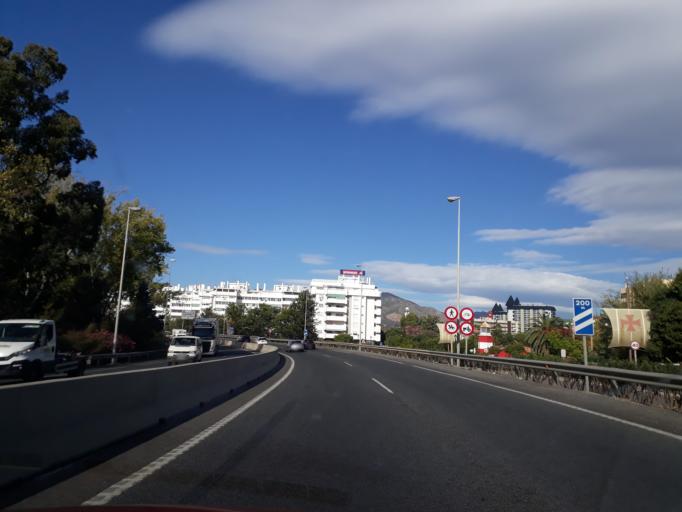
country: ES
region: Andalusia
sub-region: Provincia de Malaga
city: Fuengirola
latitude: 36.5281
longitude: -4.6287
